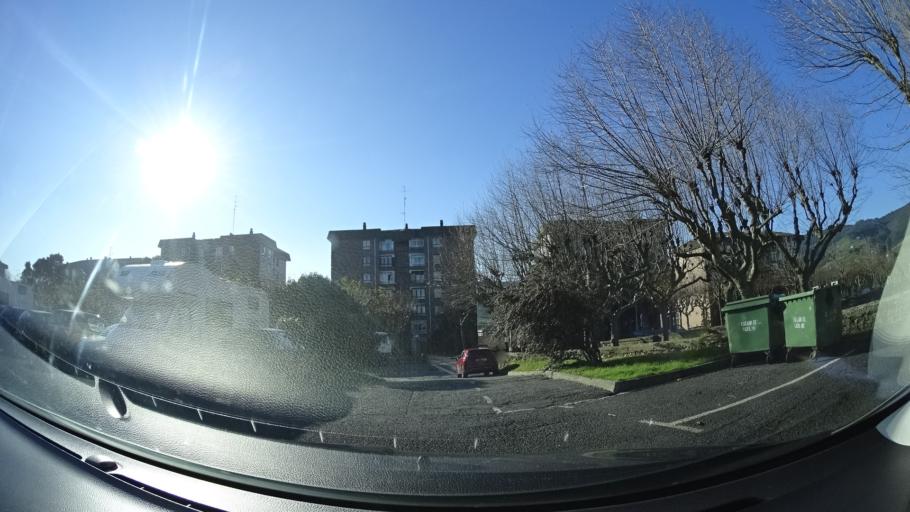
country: ES
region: Basque Country
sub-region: Bizkaia
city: Bermeo
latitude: 43.4233
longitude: -2.7269
